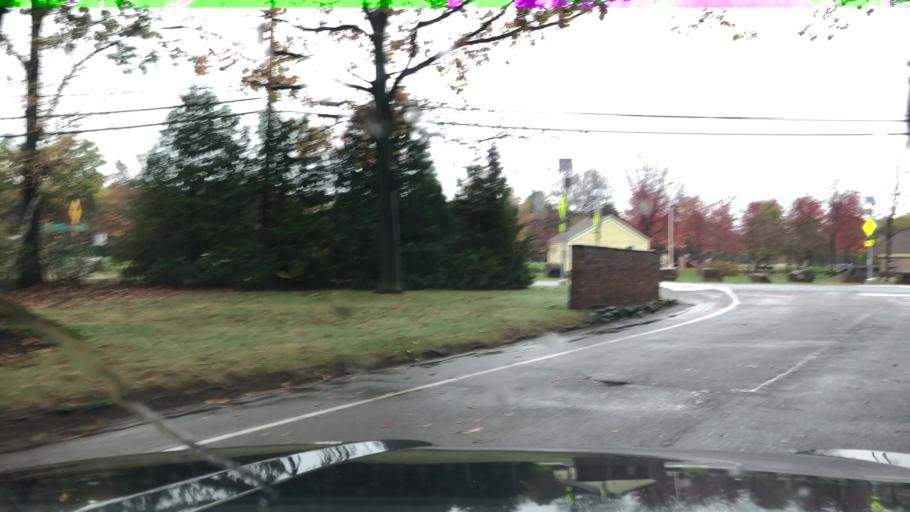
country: US
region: Vermont
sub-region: Chittenden County
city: Burlington
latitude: 44.5427
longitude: -73.2800
